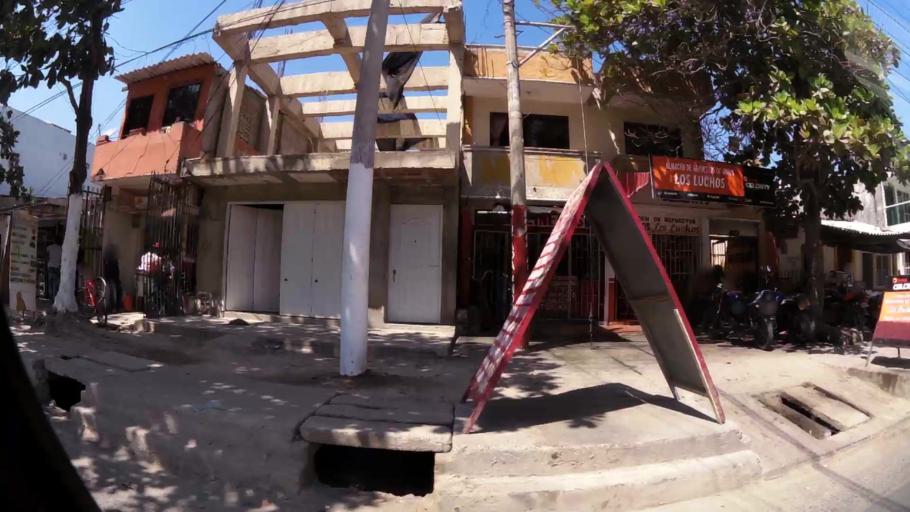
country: CO
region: Bolivar
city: Cartagena
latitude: 10.4364
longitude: -75.5277
